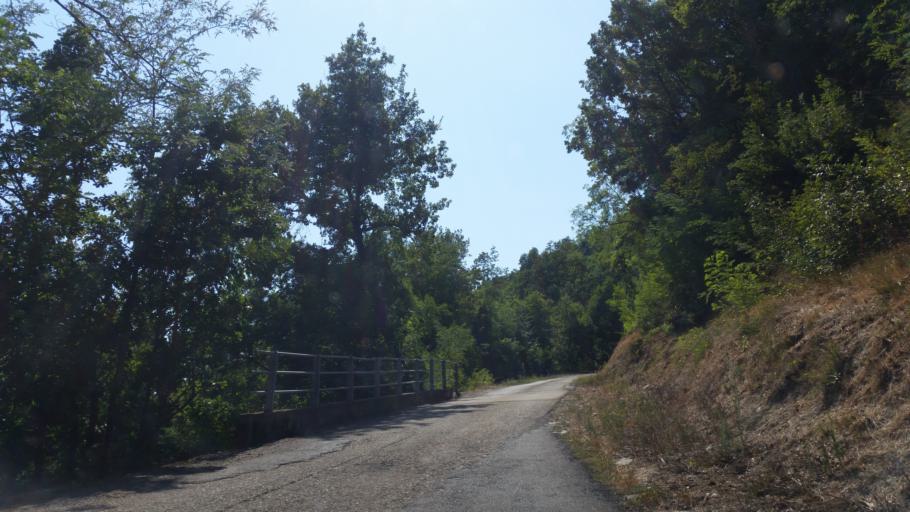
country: IT
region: Piedmont
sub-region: Provincia di Cuneo
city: Sinio
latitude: 44.5984
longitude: 8.0126
